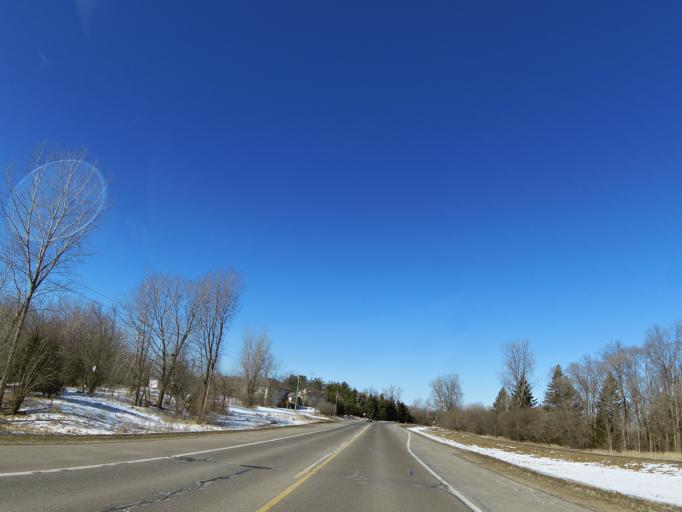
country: US
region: Minnesota
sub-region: Washington County
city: Stillwater
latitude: 45.0726
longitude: -92.8261
